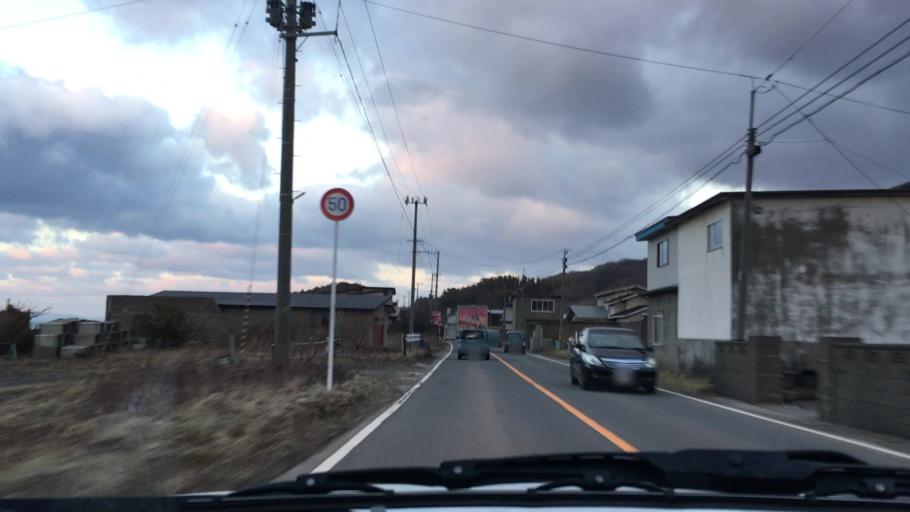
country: JP
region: Aomori
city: Shimokizukuri
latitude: 40.7540
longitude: 140.1494
